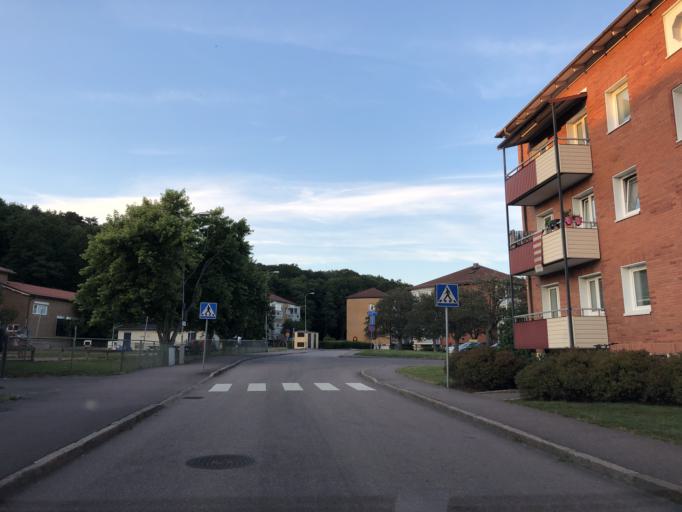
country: SE
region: Vaestra Goetaland
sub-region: Goteborg
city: Majorna
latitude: 57.7316
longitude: 11.9209
